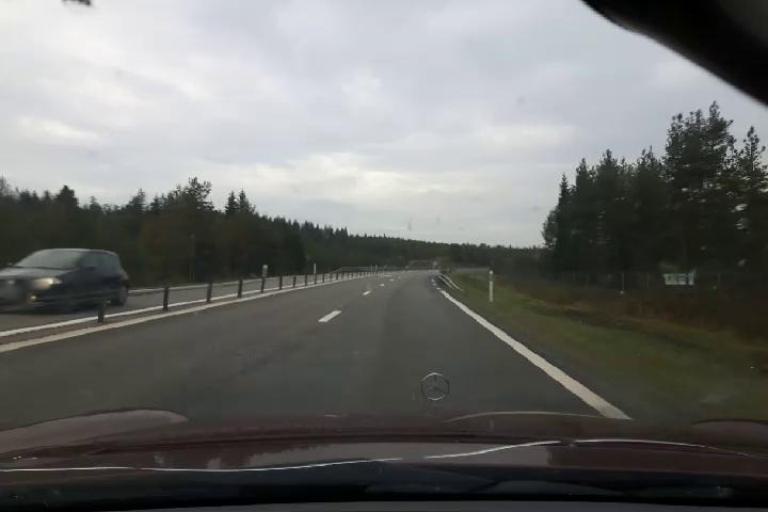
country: SE
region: Vaesternorrland
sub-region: Haernoesands Kommun
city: Haernoesand
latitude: 62.7211
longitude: 17.9190
